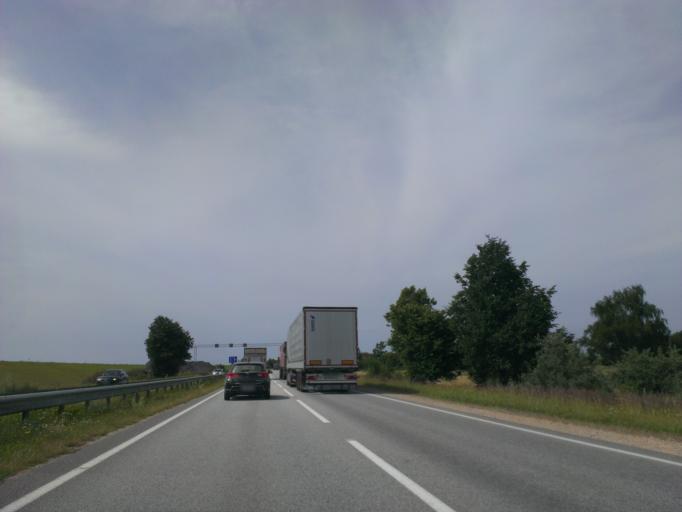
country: LV
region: Salaspils
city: Salaspils
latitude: 56.8467
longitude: 24.3642
